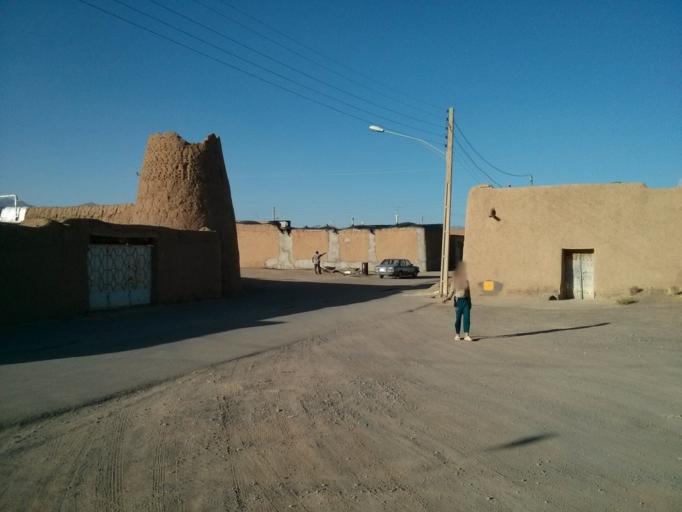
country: IR
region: Isfahan
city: Na'in
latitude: 32.7313
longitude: 52.6816
